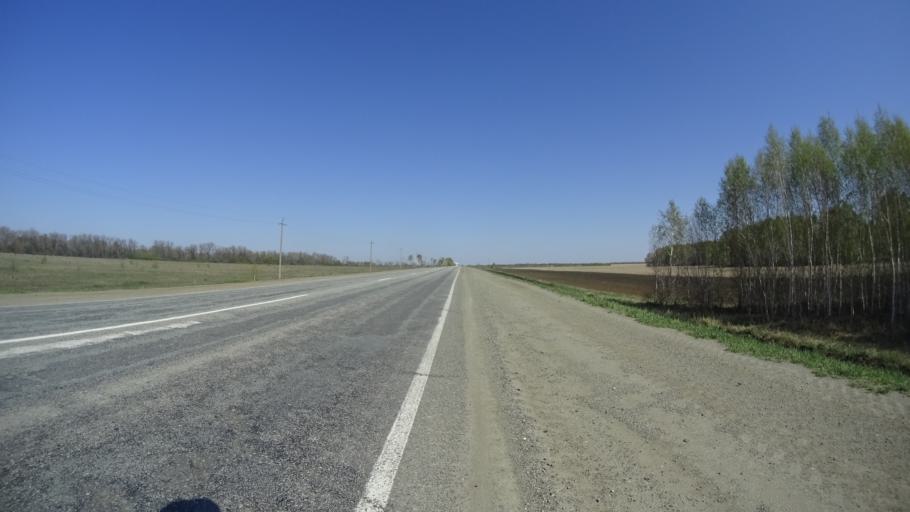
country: RU
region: Chelyabinsk
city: Troitsk
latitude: 54.1906
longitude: 61.4335
